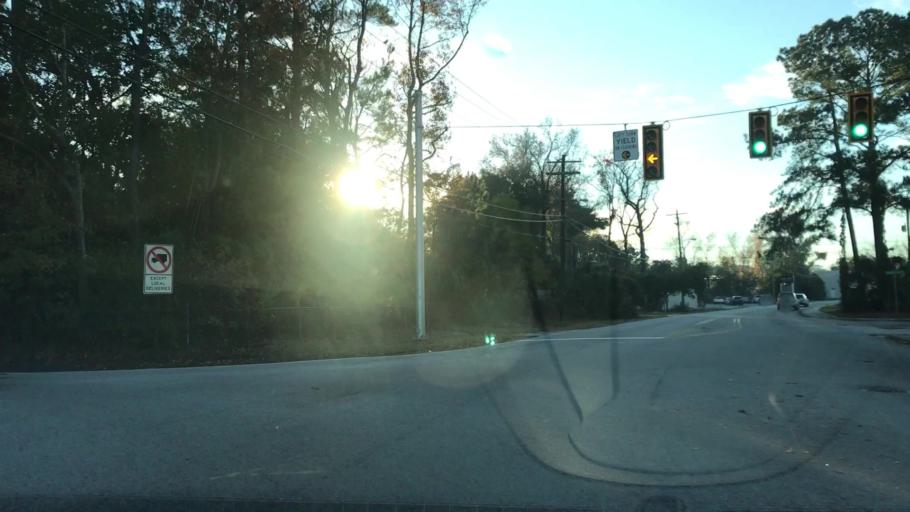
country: US
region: South Carolina
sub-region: Charleston County
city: North Charleston
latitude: 32.8104
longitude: -80.0105
